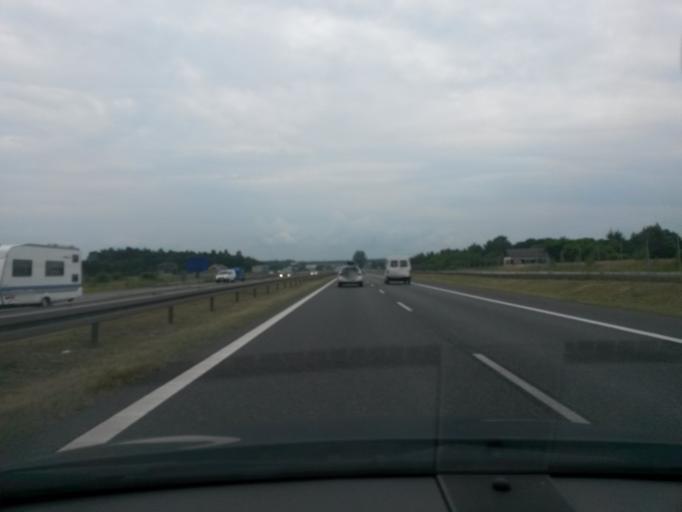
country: PL
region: Masovian Voivodeship
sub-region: Powiat zyrardowski
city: Mszczonow
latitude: 51.9498
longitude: 20.4895
